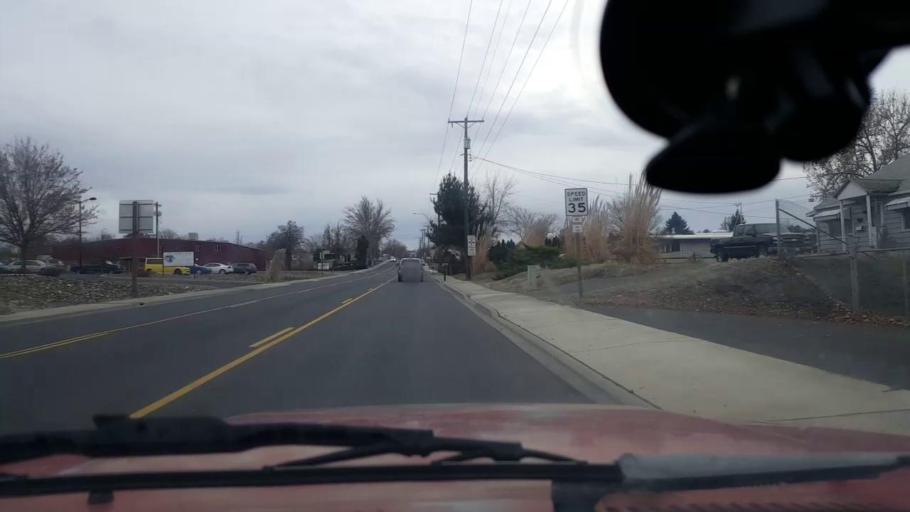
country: US
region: Washington
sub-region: Asotin County
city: West Clarkston-Highland
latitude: 46.4192
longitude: -117.0692
